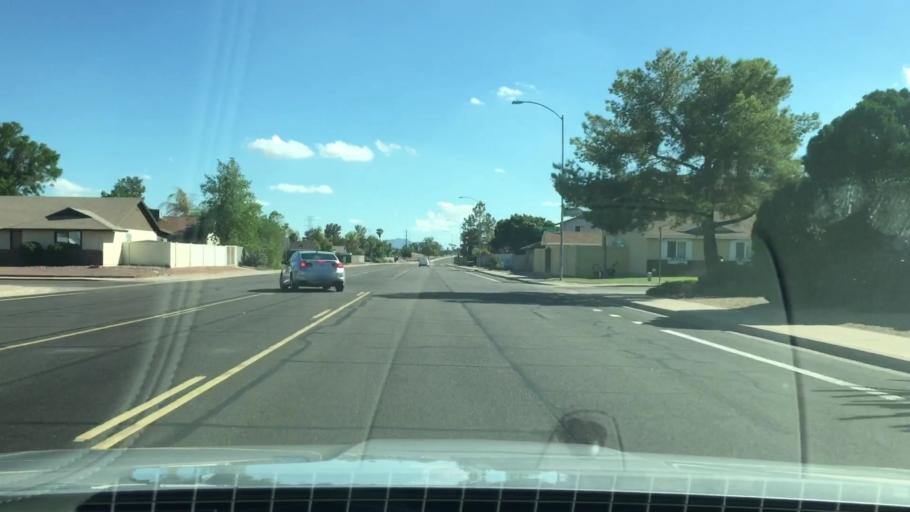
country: US
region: Arizona
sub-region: Maricopa County
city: Gilbert
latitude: 33.3919
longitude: -111.7477
